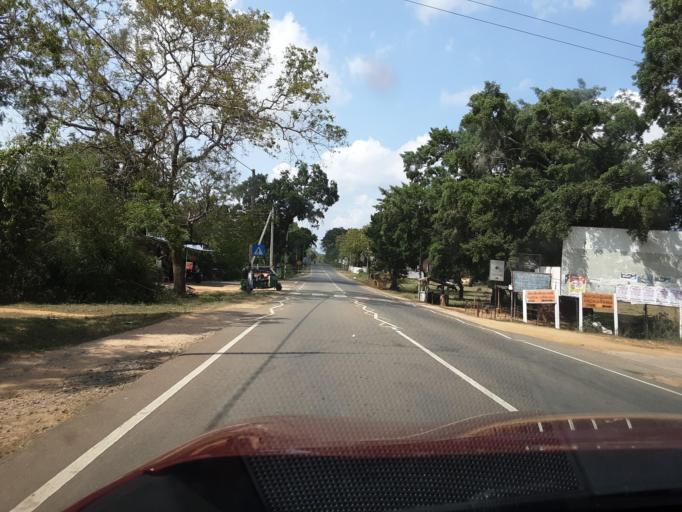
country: LK
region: Southern
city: Tangalla
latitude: 6.2716
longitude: 81.2277
